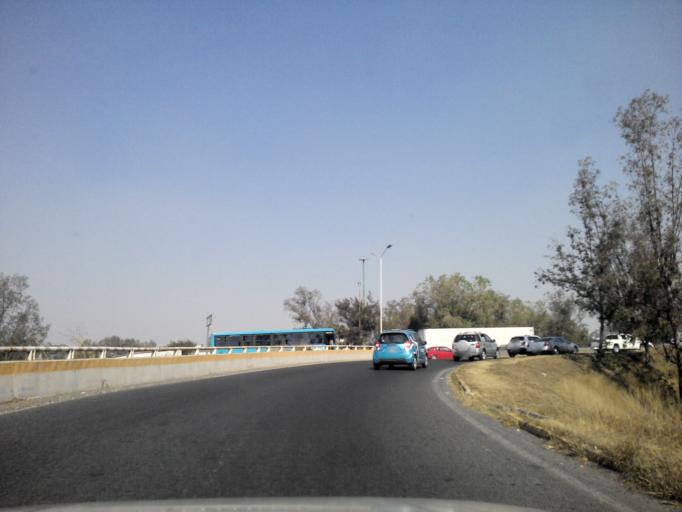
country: MX
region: Jalisco
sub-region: Tlajomulco de Zuniga
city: La Tijera
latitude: 20.6147
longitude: -103.4283
